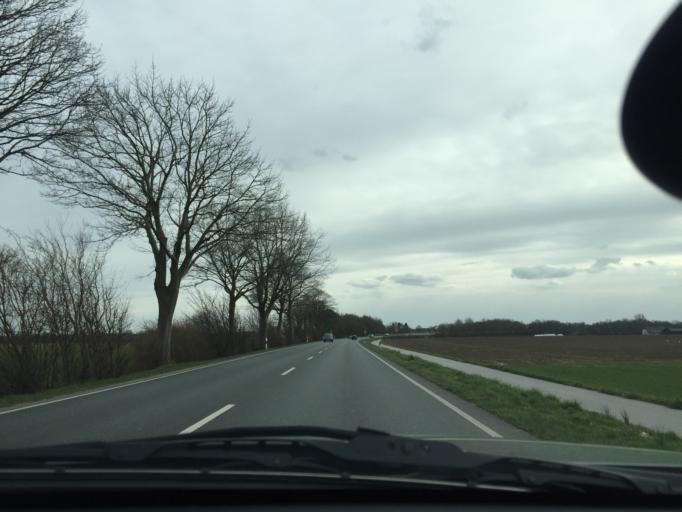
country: DE
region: North Rhine-Westphalia
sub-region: Regierungsbezirk Dusseldorf
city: Goch
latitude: 51.7227
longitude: 6.1587
